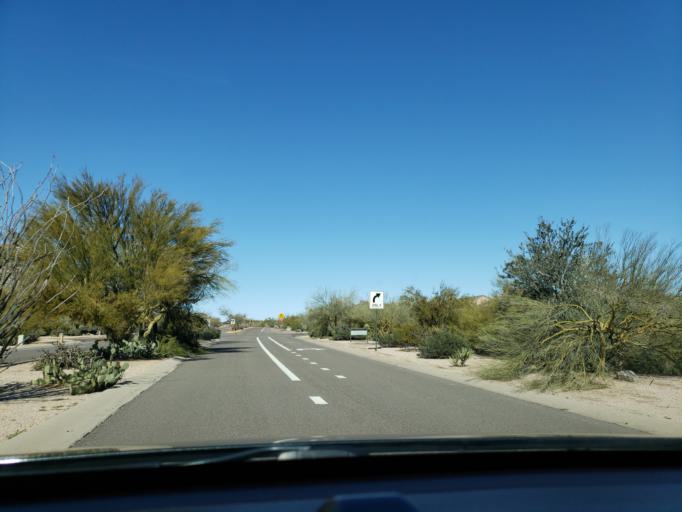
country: US
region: Arizona
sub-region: Maricopa County
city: Carefree
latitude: 33.7100
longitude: -111.8292
